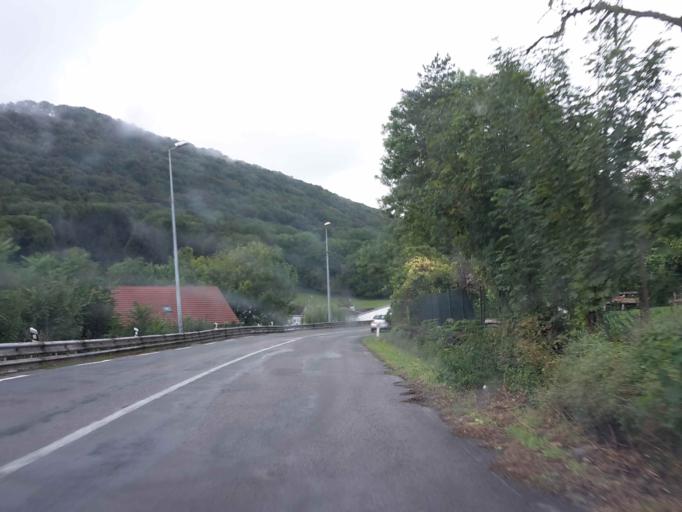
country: FR
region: Franche-Comte
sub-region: Departement du Doubs
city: Roulans
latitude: 47.3142
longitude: 6.2294
